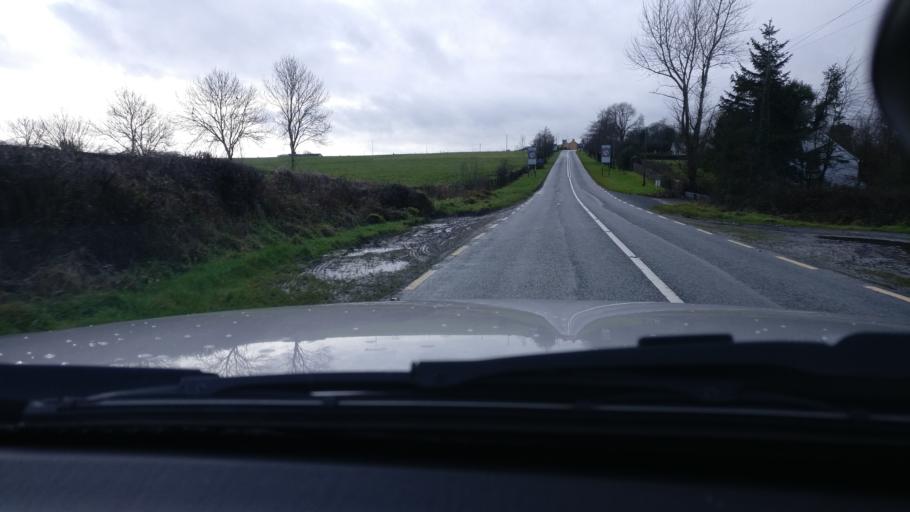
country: IE
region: Leinster
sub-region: An Longfort
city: Edgeworthstown
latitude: 53.6354
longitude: -7.6798
